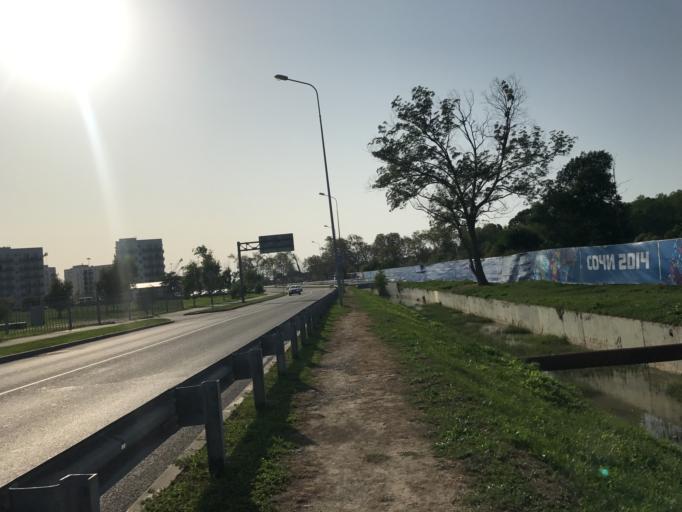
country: RU
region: Krasnodarskiy
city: Adler
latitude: 43.4144
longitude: 39.9374
